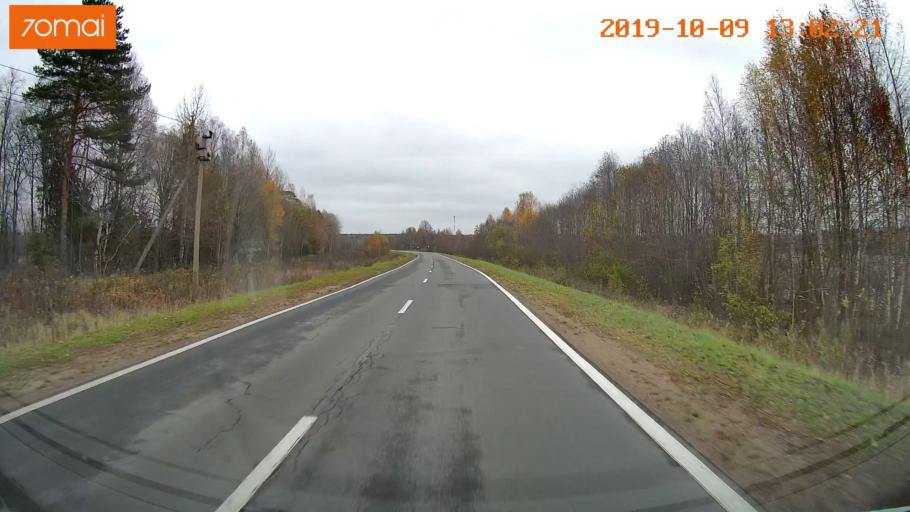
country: RU
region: Jaroslavl
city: Prechistoye
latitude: 58.3620
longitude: 40.4993
